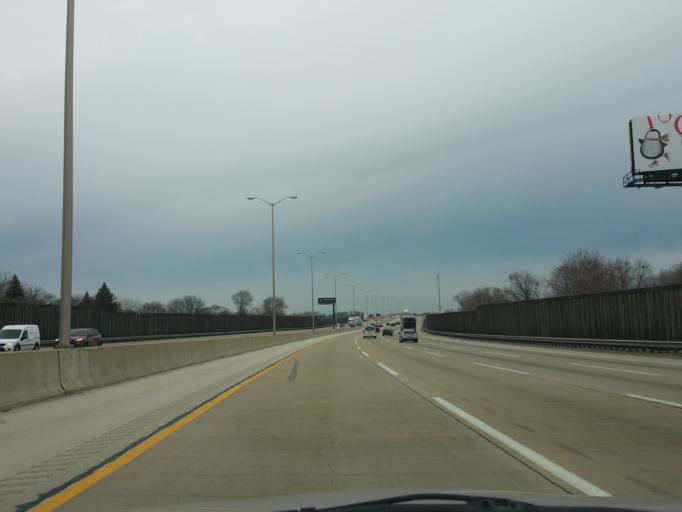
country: US
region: Illinois
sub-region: Cook County
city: Chicago Ridge
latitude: 41.6916
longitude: -87.7835
